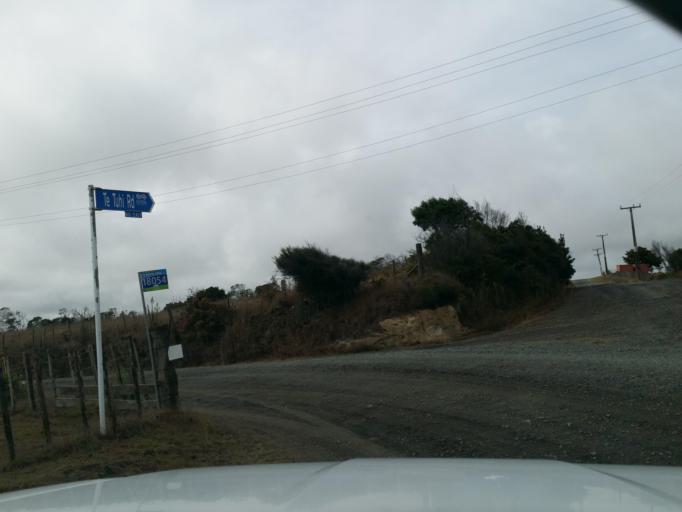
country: NZ
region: Northland
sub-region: Kaipara District
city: Dargaville
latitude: -36.0062
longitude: 173.8814
